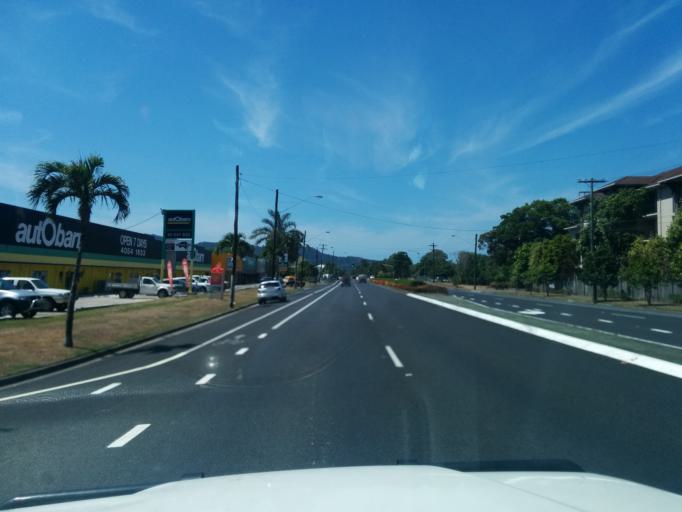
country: AU
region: Queensland
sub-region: Cairns
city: Woree
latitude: -16.9335
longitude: 145.7431
